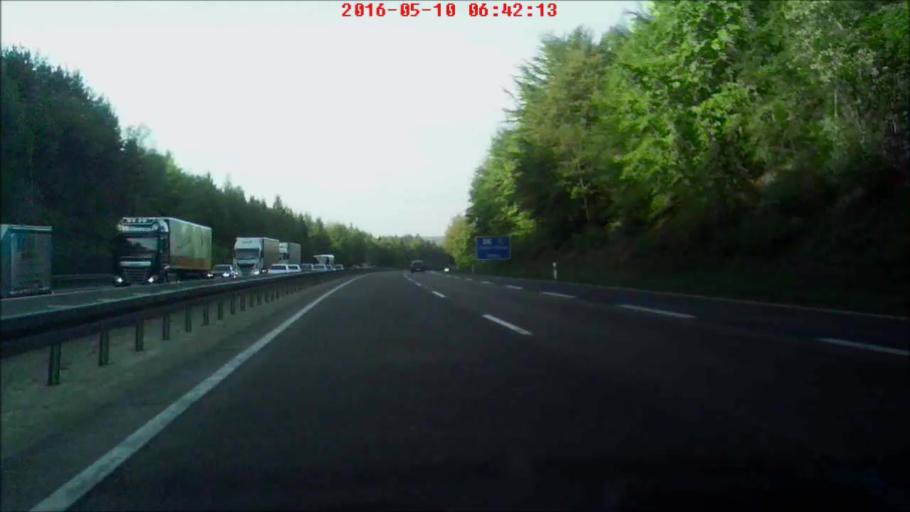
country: DE
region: Hesse
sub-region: Regierungsbezirk Kassel
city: Kunzell
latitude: 50.5071
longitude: 9.7381
